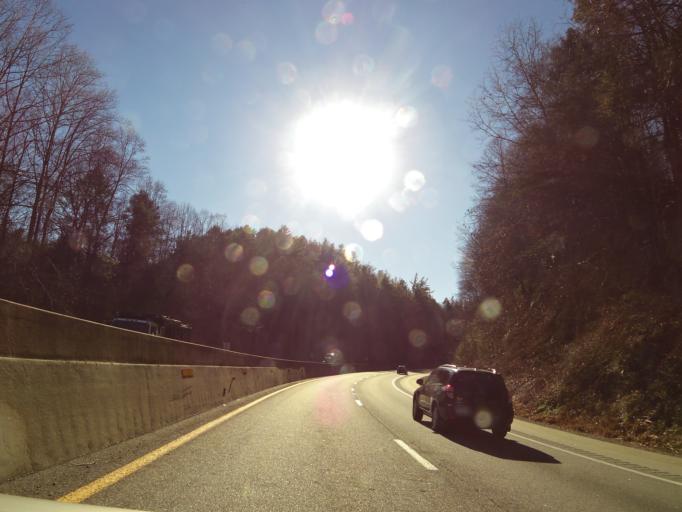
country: US
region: North Carolina
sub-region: Haywood County
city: Cove Creek
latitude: 35.6866
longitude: -83.0302
